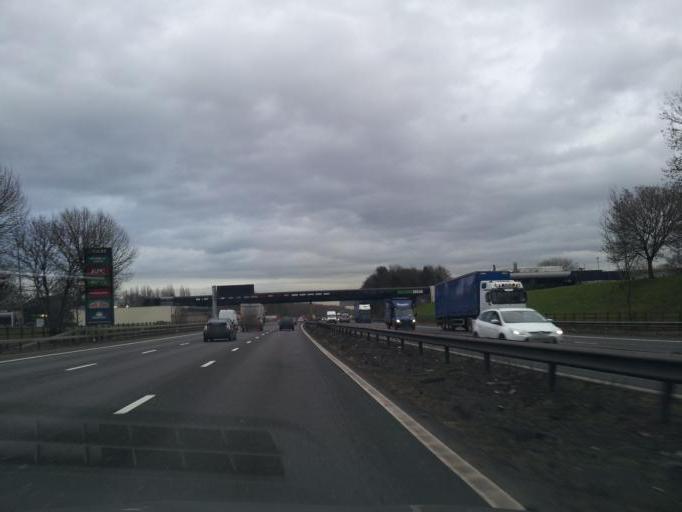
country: GB
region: England
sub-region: Coventry
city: Keresley
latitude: 52.4717
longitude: -1.5491
